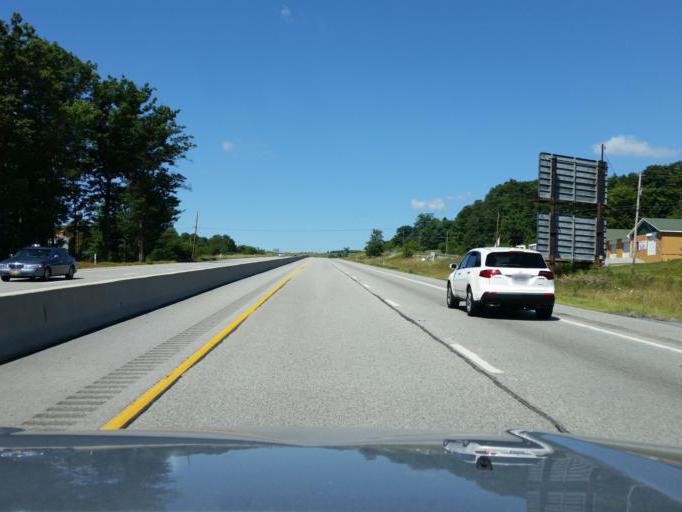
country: US
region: Pennsylvania
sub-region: Cambria County
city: Mundys Corner
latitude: 40.4509
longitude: -78.8528
